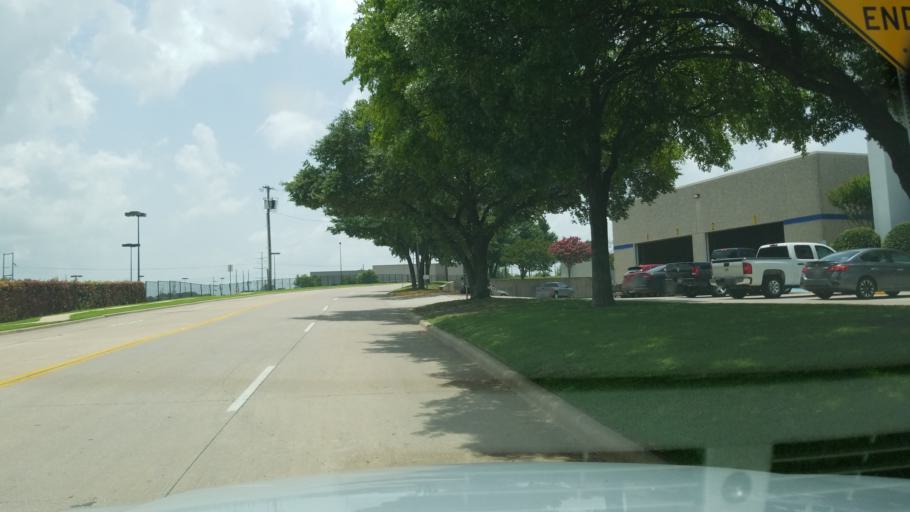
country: US
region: Texas
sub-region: Dallas County
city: Irving
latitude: 32.8191
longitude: -96.9097
